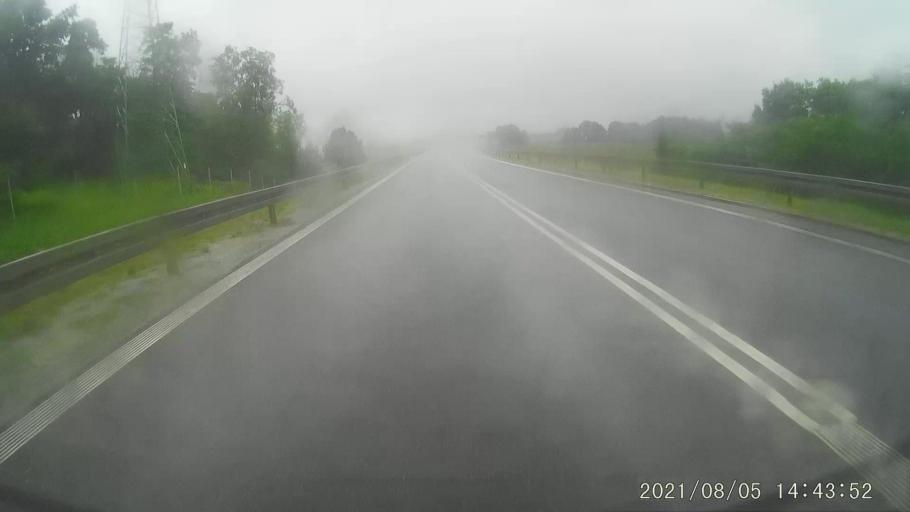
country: PL
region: Opole Voivodeship
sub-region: Powiat nyski
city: Nysa
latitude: 50.4887
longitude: 17.3866
